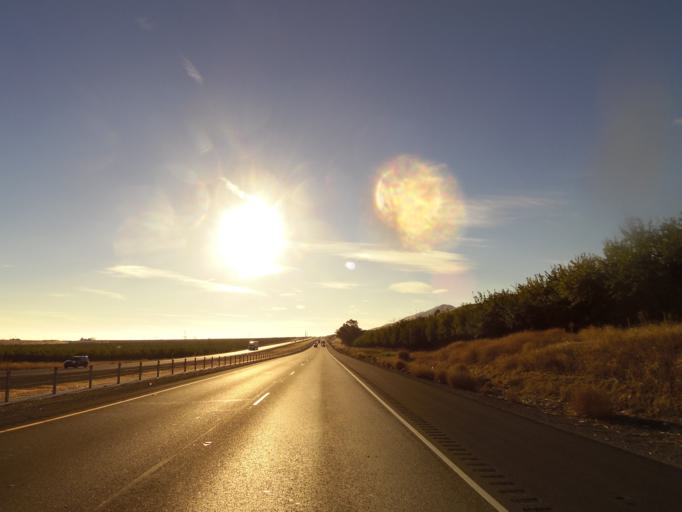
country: US
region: California
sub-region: Stanislaus County
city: Patterson
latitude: 37.5279
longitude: -121.2528
